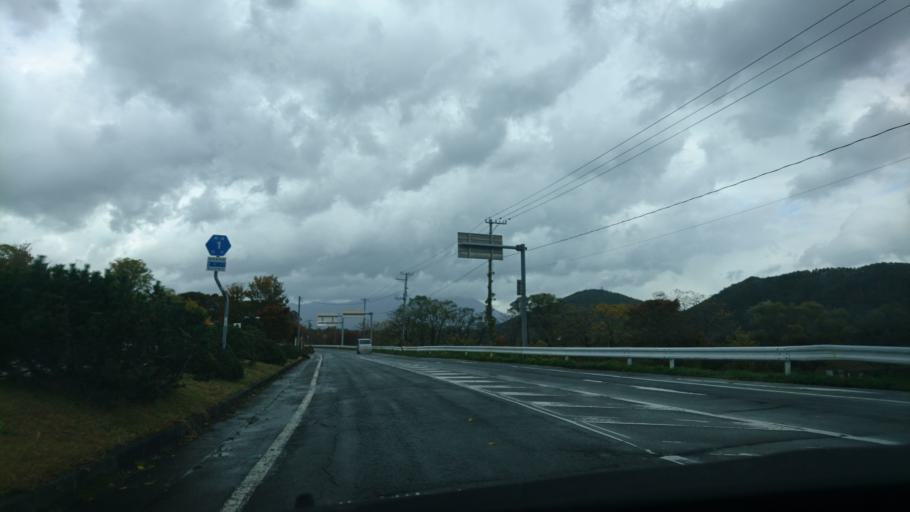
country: JP
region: Iwate
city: Shizukuishi
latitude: 39.6767
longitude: 140.9923
